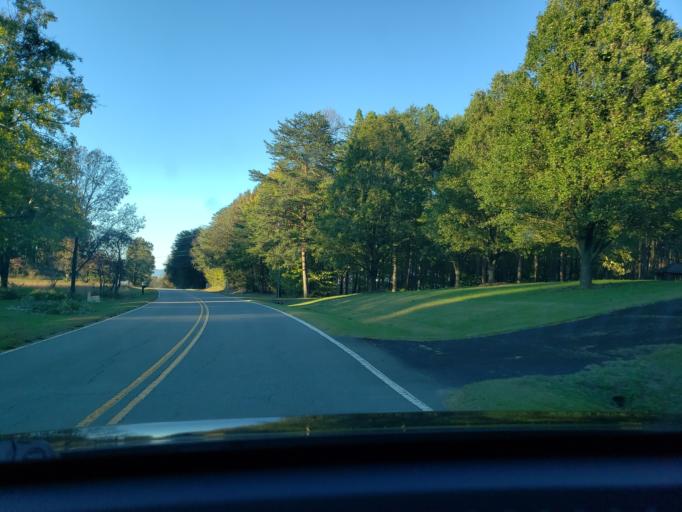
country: US
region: North Carolina
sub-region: Forsyth County
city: Walkertown
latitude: 36.2280
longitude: -80.1984
